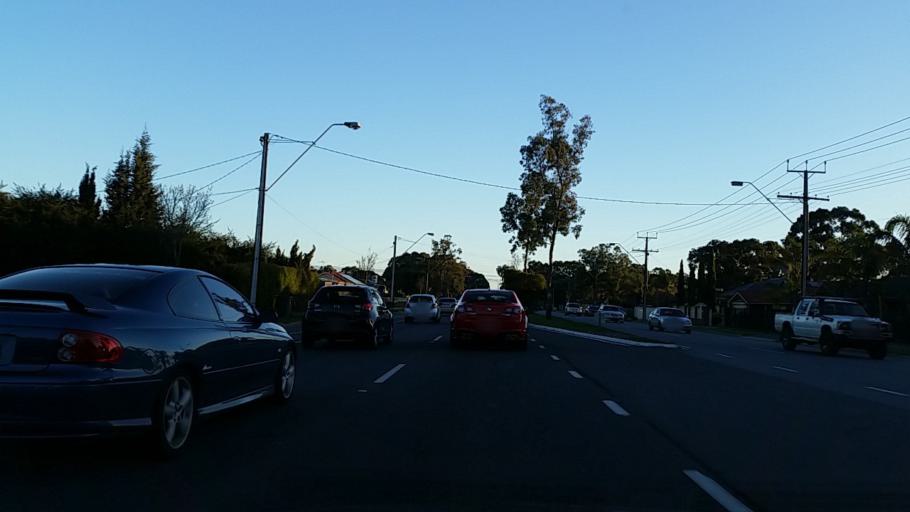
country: AU
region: South Australia
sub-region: Salisbury
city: Salisbury
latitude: -34.7942
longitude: 138.6130
